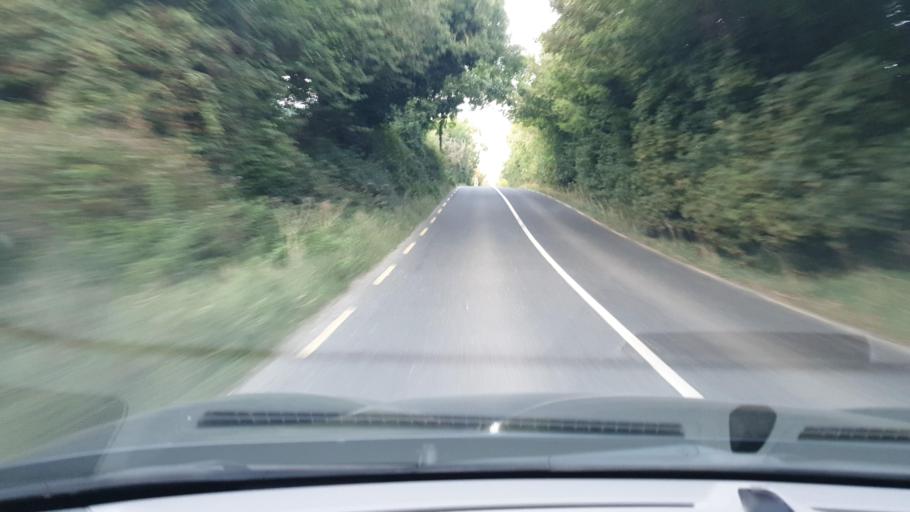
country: IE
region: Leinster
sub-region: An Mhi
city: Stamullin
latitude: 53.5947
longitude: -6.2663
